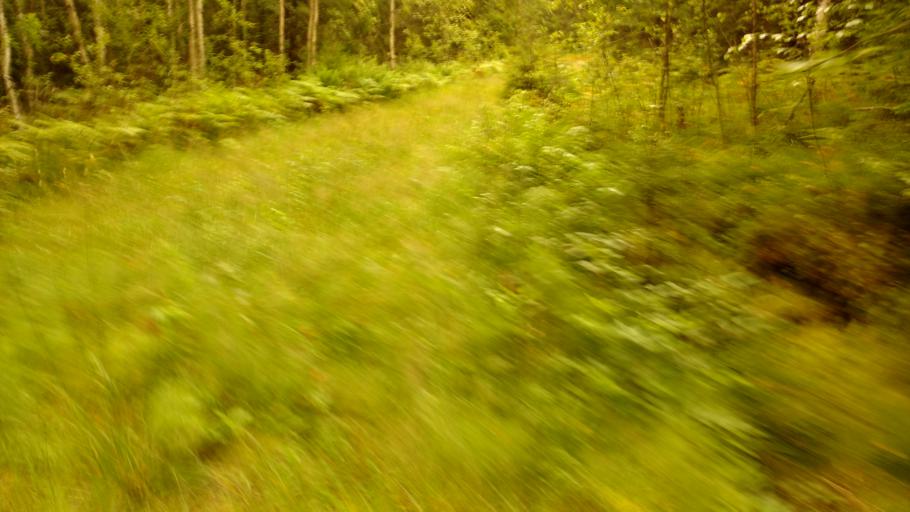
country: FI
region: Varsinais-Suomi
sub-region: Salo
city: Pertteli
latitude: 60.4062
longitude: 23.2352
